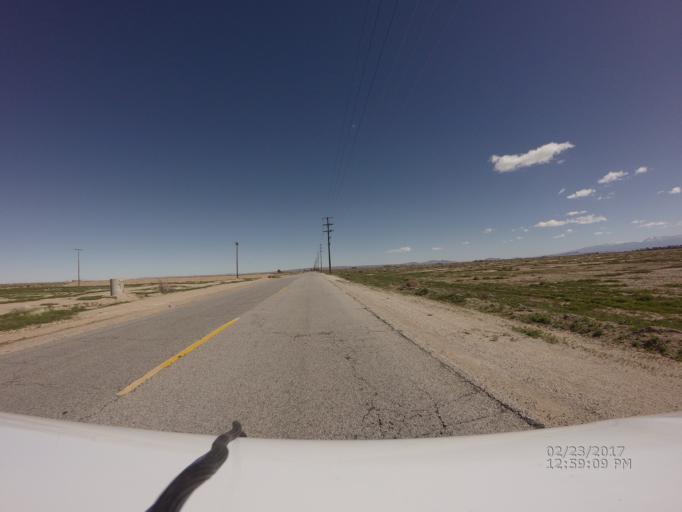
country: US
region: California
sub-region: Los Angeles County
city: Lancaster
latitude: 34.7630
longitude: -118.0375
